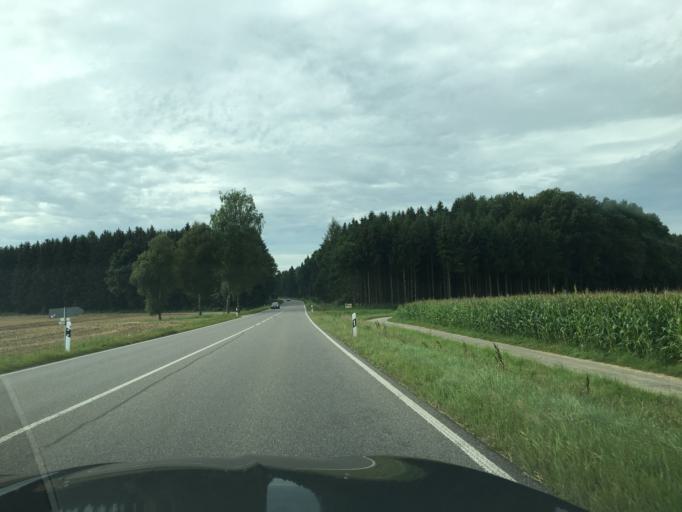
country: DE
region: Baden-Wuerttemberg
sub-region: Tuebingen Region
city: Emeringen
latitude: 48.2034
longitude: 9.5319
